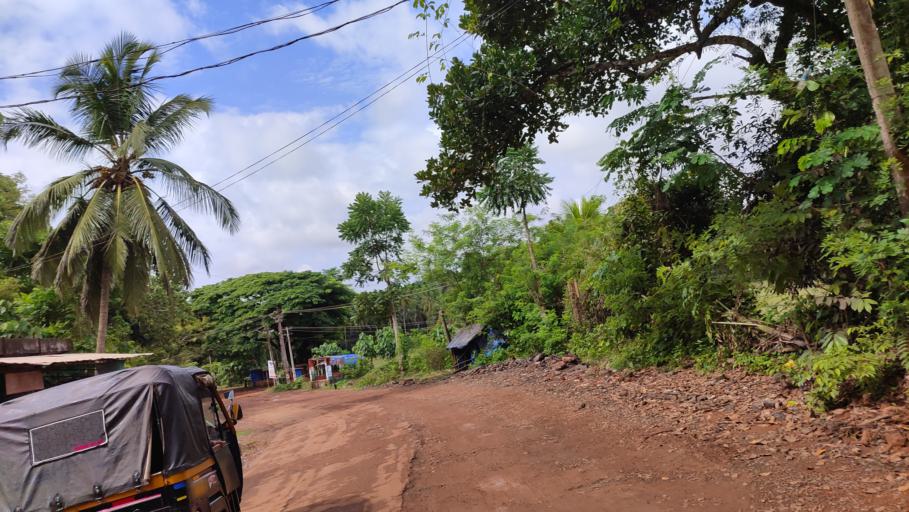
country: IN
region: Kerala
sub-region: Kasaragod District
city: Kasaragod
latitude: 12.5242
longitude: 75.0716
